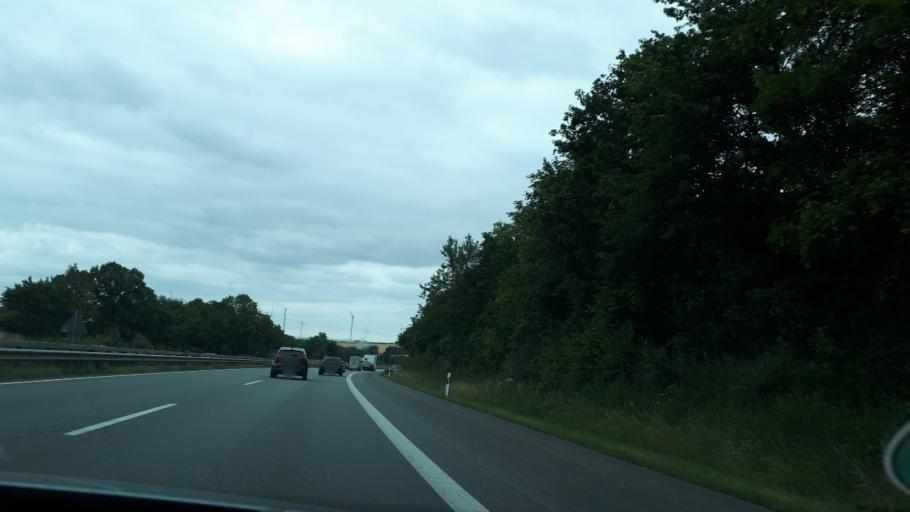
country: DE
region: Rheinland-Pfalz
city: Kaifenheim
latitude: 50.2423
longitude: 7.2159
